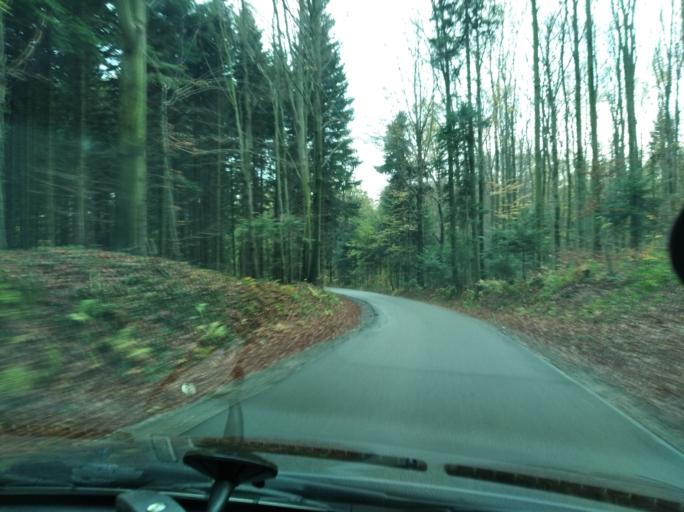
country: PL
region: Subcarpathian Voivodeship
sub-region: Powiat strzyzowski
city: Strzyzow
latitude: 49.9018
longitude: 21.7845
